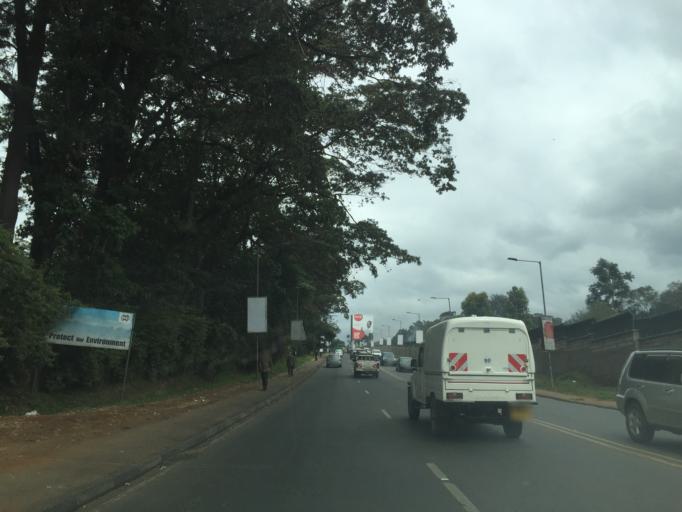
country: KE
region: Nairobi Area
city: Nairobi
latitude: -1.2924
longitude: 36.8051
